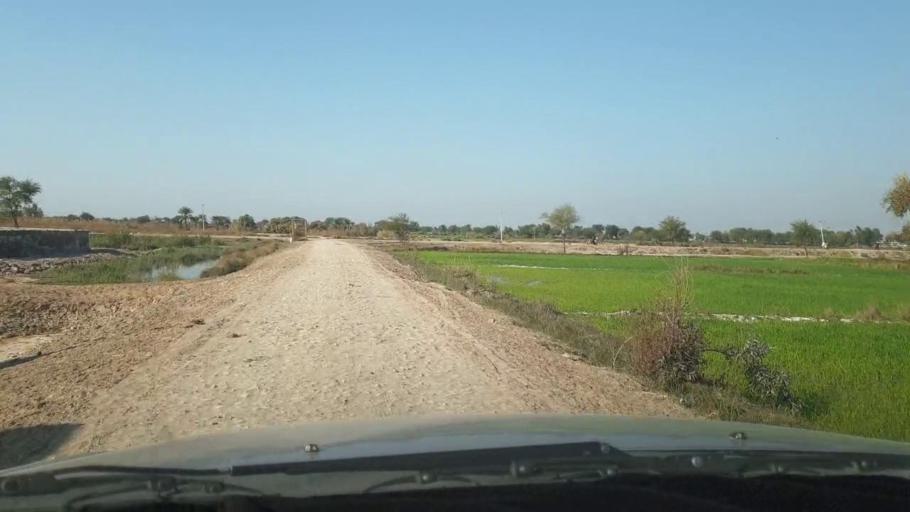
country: PK
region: Sindh
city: Mirpur Mathelo
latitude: 27.9826
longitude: 69.5356
